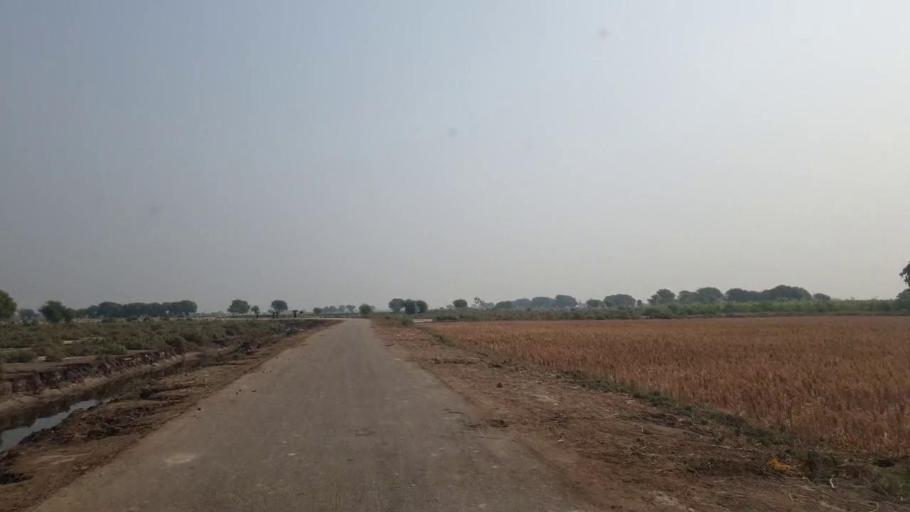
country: PK
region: Sindh
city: Matli
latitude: 25.1304
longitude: 68.6974
